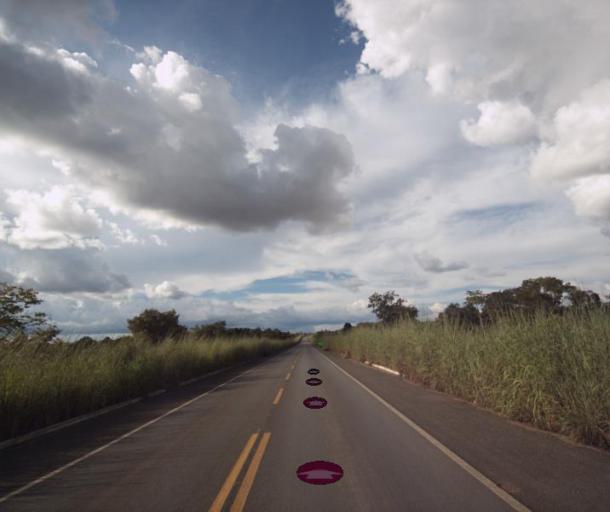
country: BR
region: Goias
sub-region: Barro Alto
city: Barro Alto
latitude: -14.7859
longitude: -48.6307
